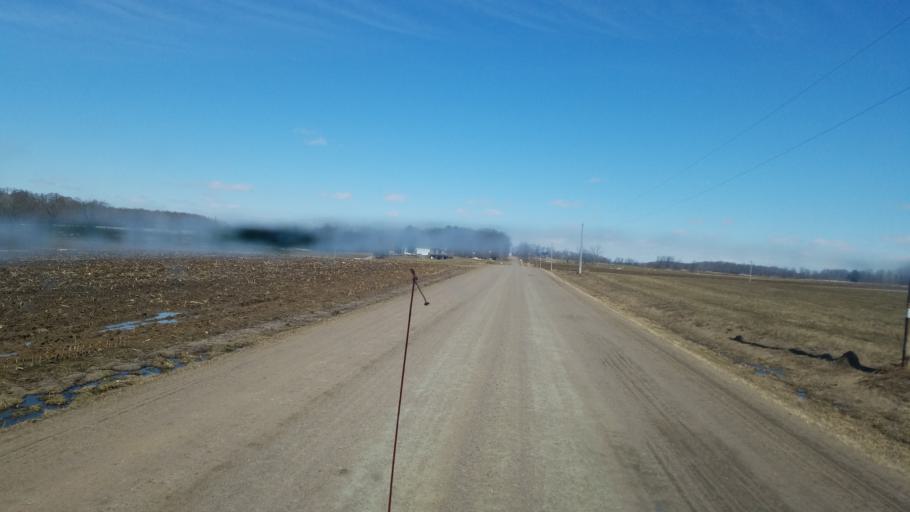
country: US
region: Wisconsin
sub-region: Clark County
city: Loyal
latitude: 44.6234
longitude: -90.3971
